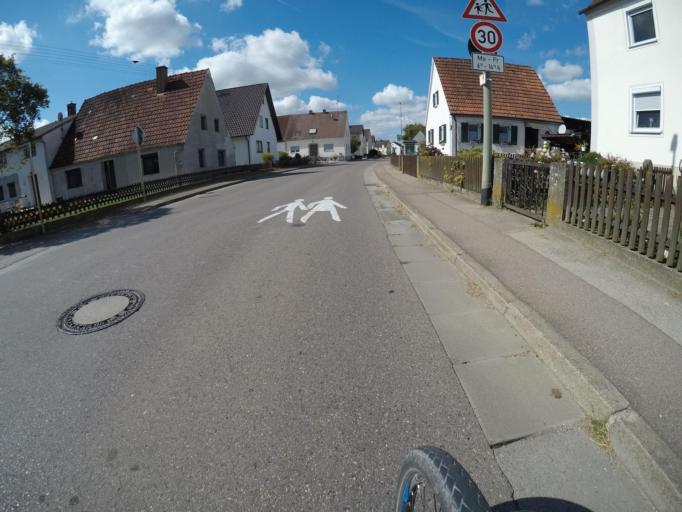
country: DE
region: Bavaria
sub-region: Swabia
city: Finningen
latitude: 48.6227
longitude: 10.5142
